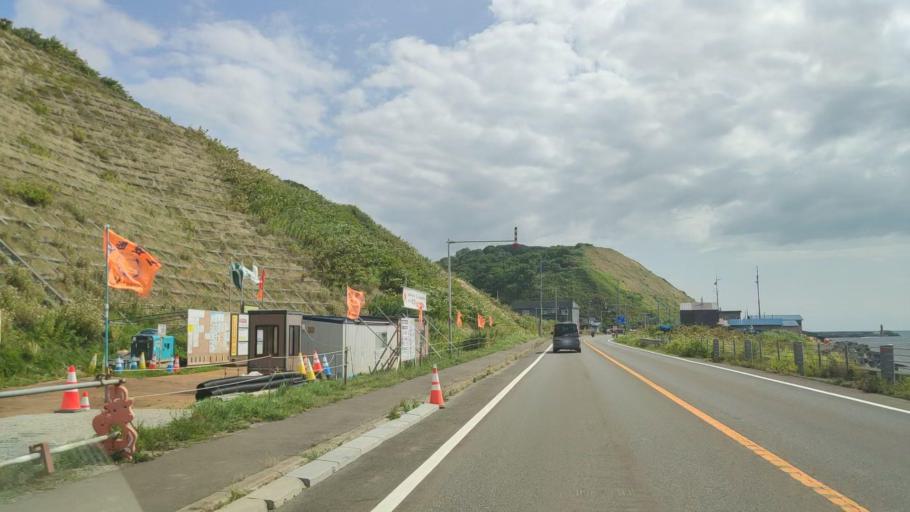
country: JP
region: Hokkaido
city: Rumoi
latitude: 44.2313
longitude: 141.6566
